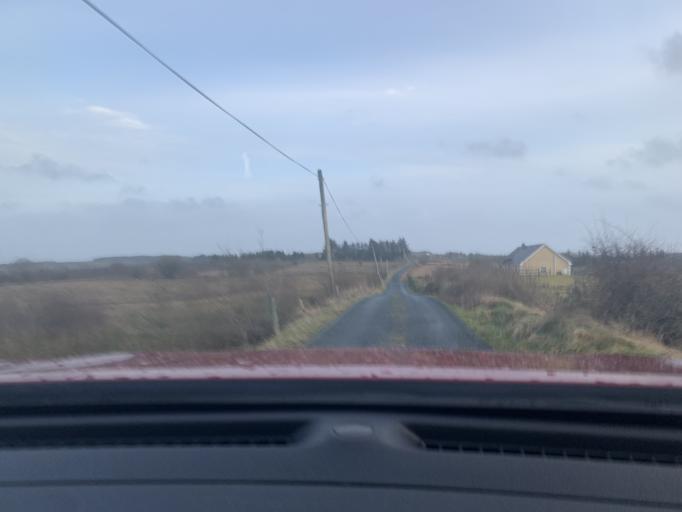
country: IE
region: Connaught
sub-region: Roscommon
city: Ballaghaderreen
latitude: 53.9588
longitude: -8.5389
